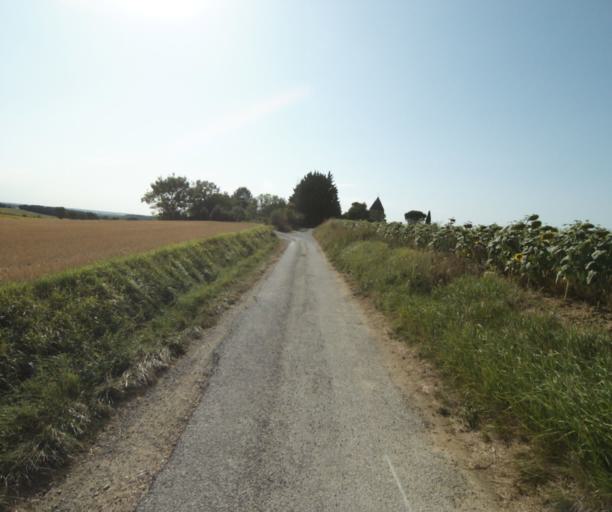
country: FR
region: Midi-Pyrenees
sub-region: Departement de la Haute-Garonne
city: Avignonet-Lauragais
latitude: 43.4288
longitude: 1.8158
